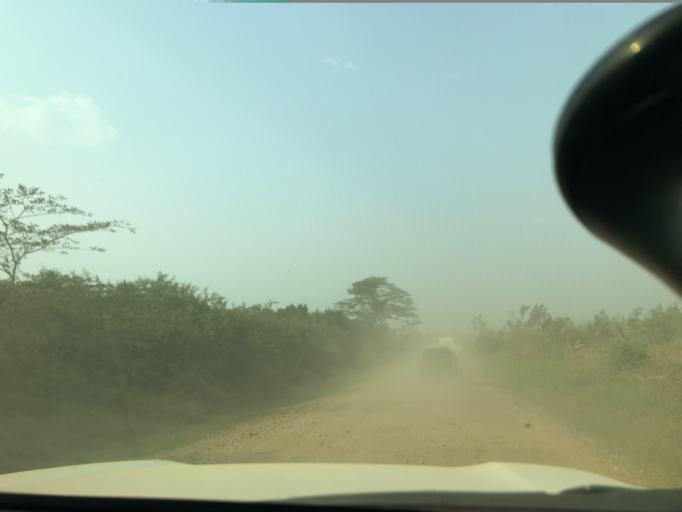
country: CD
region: Nord Kivu
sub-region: North Kivu
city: Butembo
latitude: 0.1354
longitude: 29.6424
